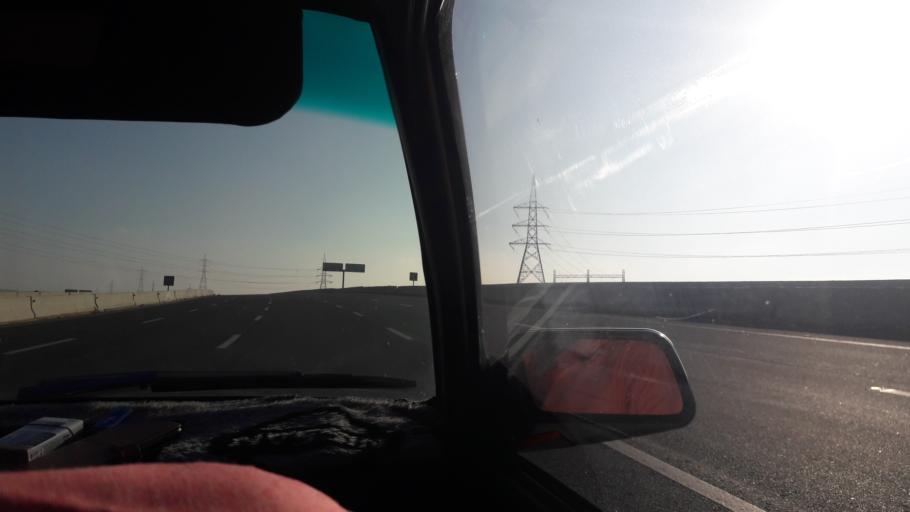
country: EG
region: Muhafazat al Qahirah
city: Halwan
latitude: 29.9227
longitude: 31.5227
